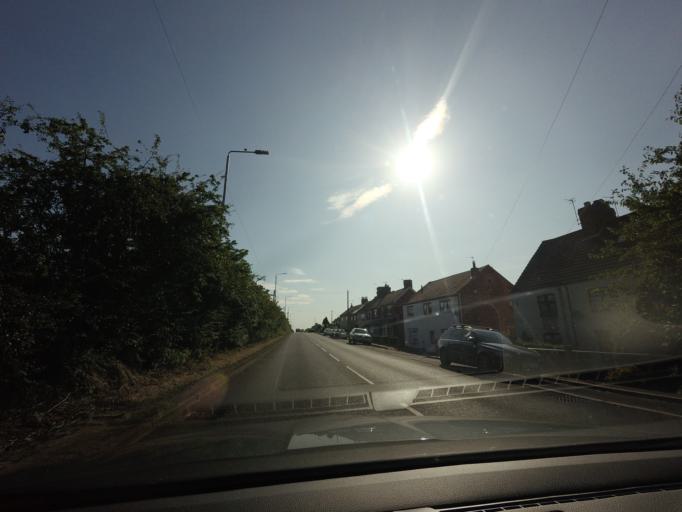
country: GB
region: England
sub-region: Derbyshire
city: Pinxton
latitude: 53.0530
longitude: -1.2902
